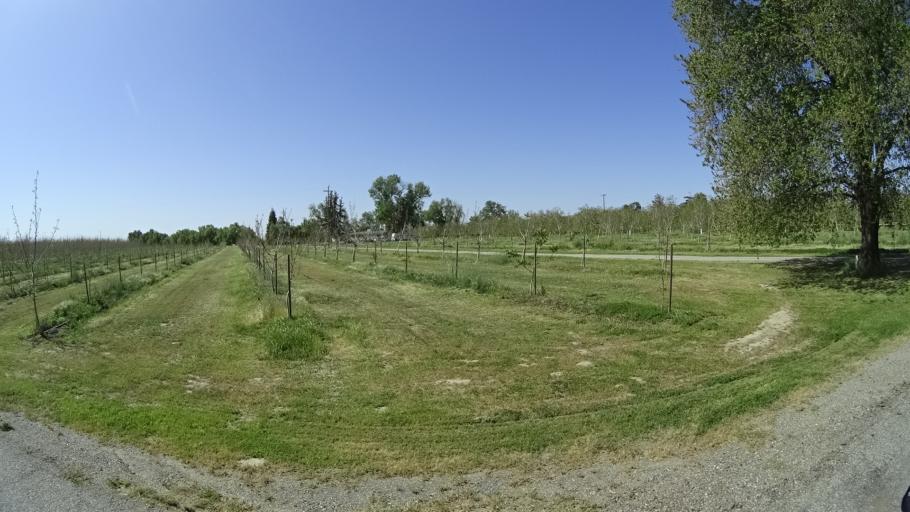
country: US
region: California
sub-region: Glenn County
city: Hamilton City
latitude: 39.7224
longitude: -122.0248
